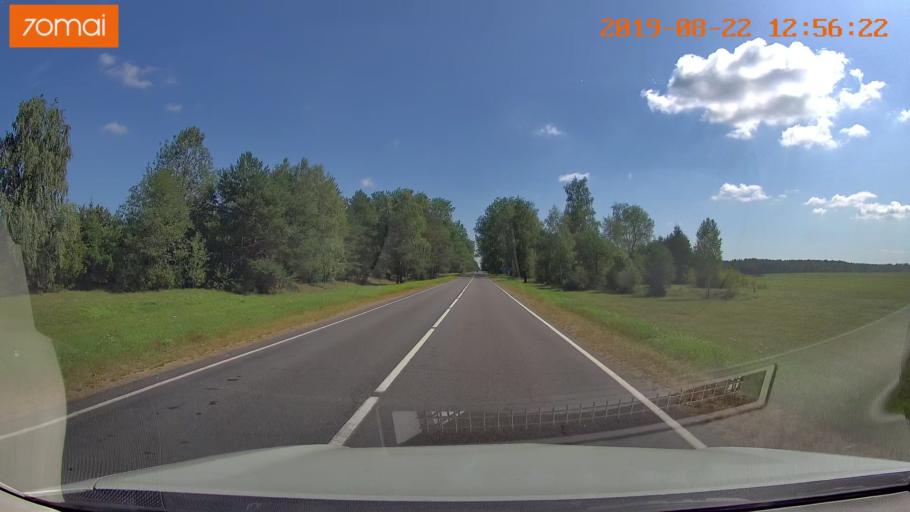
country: BY
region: Minsk
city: Prawdzinski
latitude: 53.4332
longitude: 27.7298
